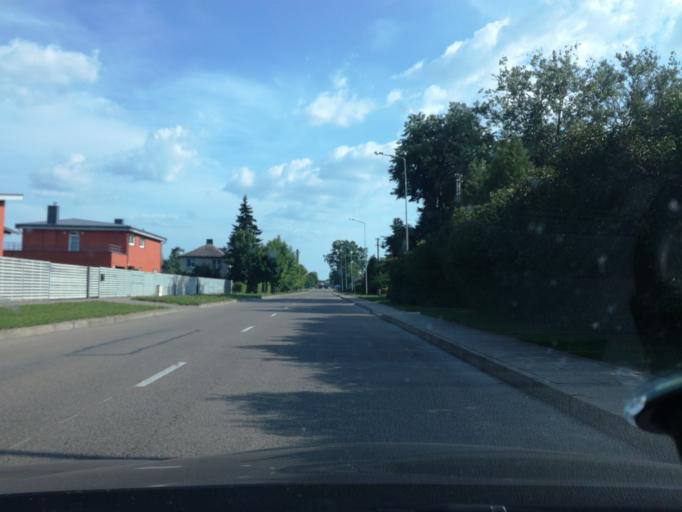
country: LT
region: Marijampoles apskritis
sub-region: Marijampole Municipality
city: Marijampole
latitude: 54.5438
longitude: 23.3486
